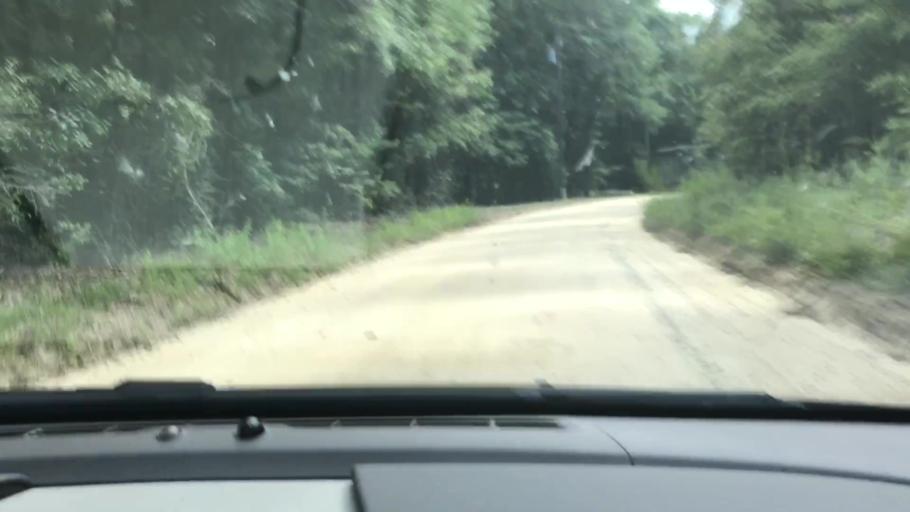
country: US
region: Georgia
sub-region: Clay County
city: Fort Gaines
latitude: 31.7333
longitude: -85.0883
